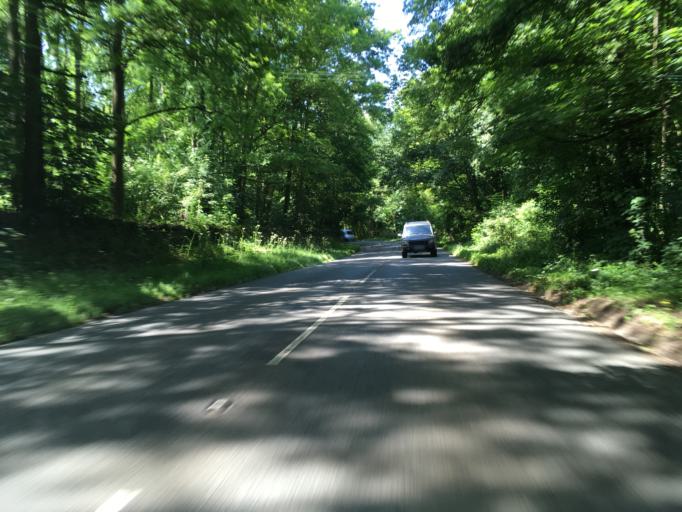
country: GB
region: England
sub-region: Gloucestershire
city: Moreton in Marsh
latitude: 51.9394
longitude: -1.6400
